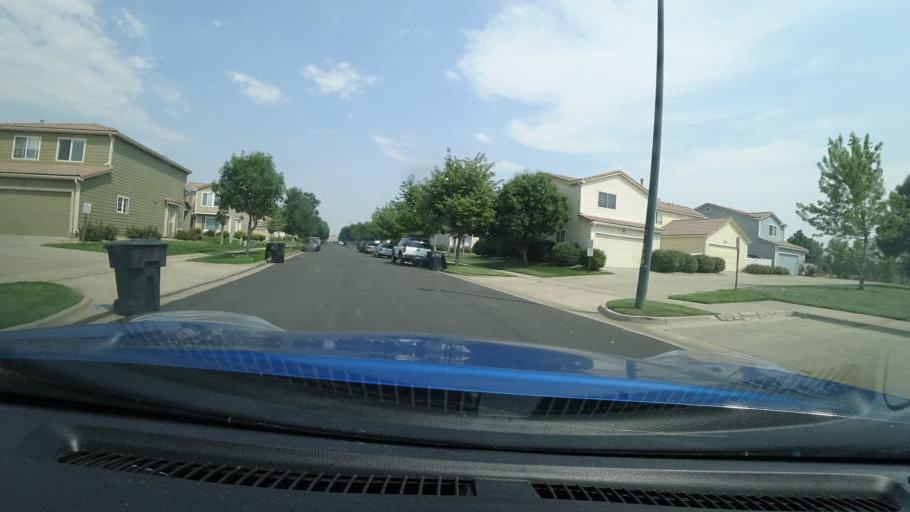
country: US
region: Colorado
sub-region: Adams County
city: Aurora
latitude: 39.7801
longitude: -104.7389
